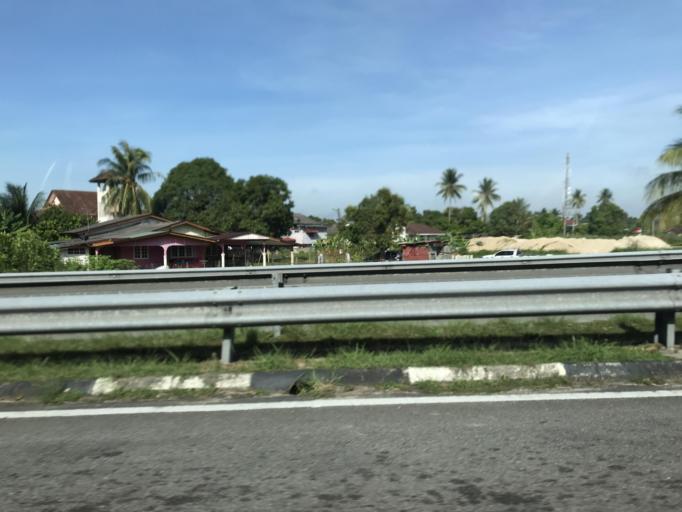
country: MY
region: Kelantan
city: Kampong Kadok
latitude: 6.0503
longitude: 102.2186
